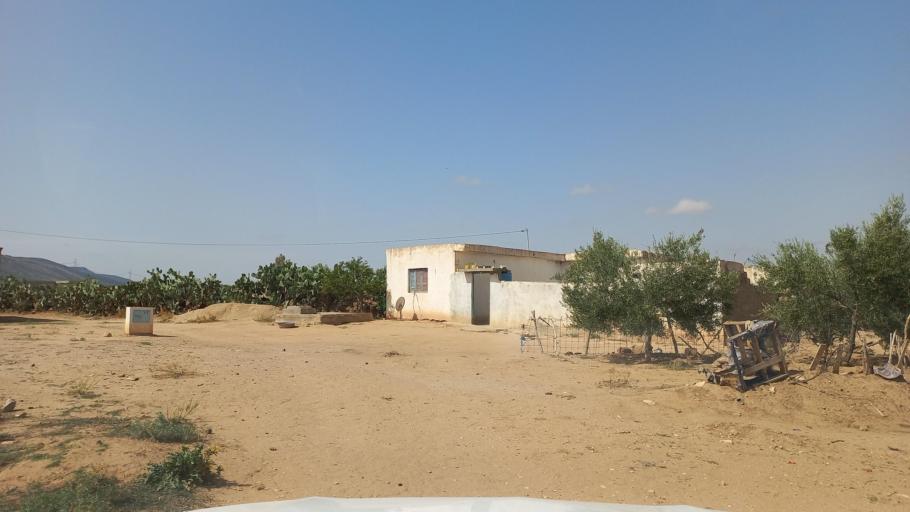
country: TN
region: Al Qasrayn
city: Sbiba
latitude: 35.3876
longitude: 8.9634
